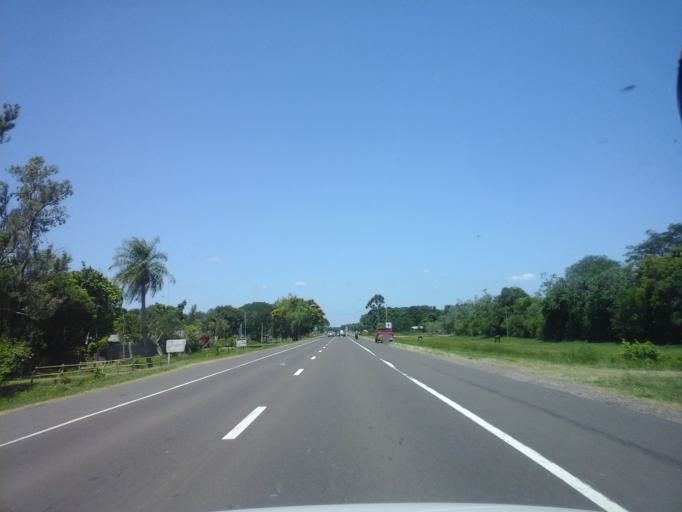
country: AR
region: Corrientes
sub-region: Departamento de San Cosme
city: San Cosme
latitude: -27.3760
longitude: -58.4967
